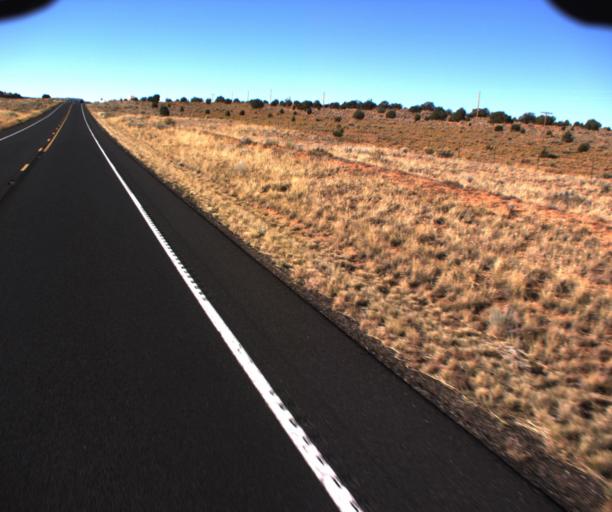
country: US
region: Arizona
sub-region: Coconino County
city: LeChee
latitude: 36.6967
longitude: -111.6017
